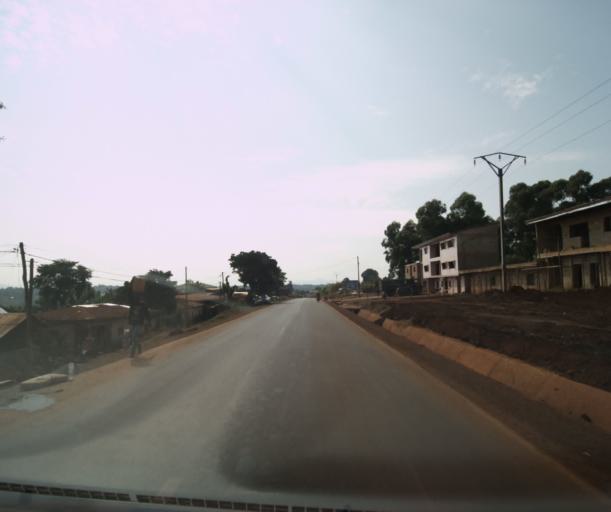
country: CM
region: West
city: Mbouda
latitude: 5.6199
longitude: 10.2706
